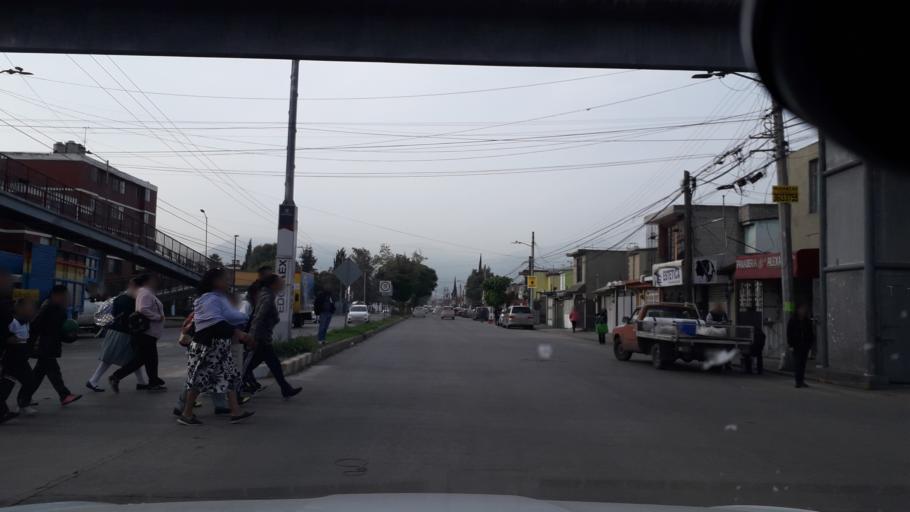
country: MX
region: Mexico
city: San Pablo de las Salinas
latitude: 19.6555
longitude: -99.0842
